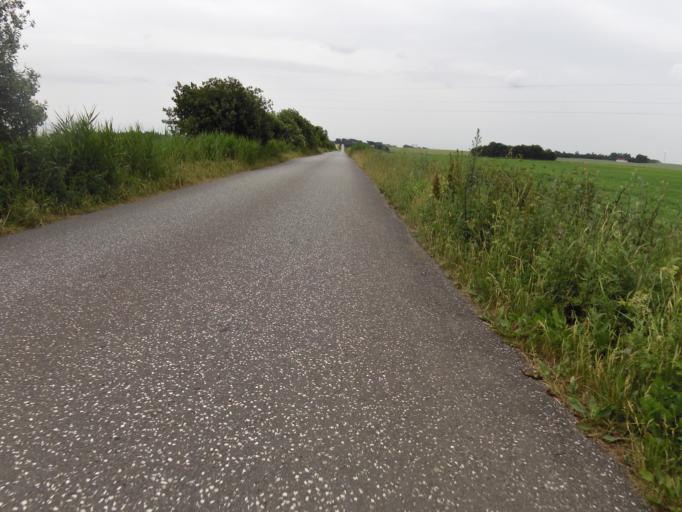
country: DK
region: Central Jutland
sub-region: Holstebro Kommune
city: Holstebro
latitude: 56.4204
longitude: 8.6745
